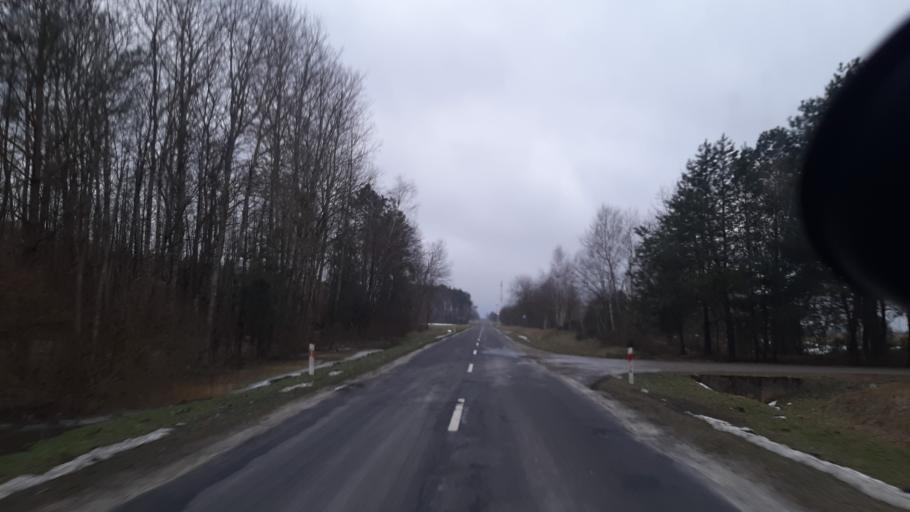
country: PL
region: Lublin Voivodeship
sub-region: Powiat wlodawski
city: Hansk
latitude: 51.5603
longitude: 23.3311
